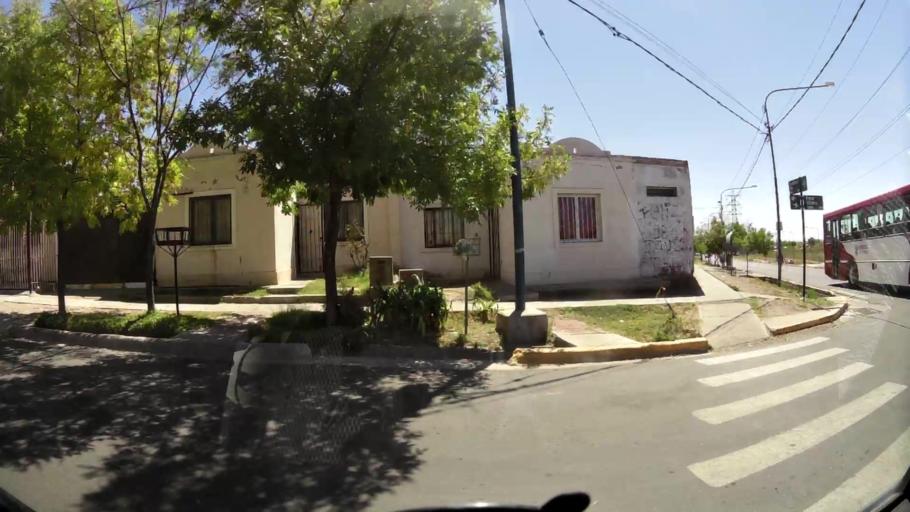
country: AR
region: Mendoza
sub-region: Departamento de Godoy Cruz
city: Godoy Cruz
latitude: -32.9402
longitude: -68.8713
